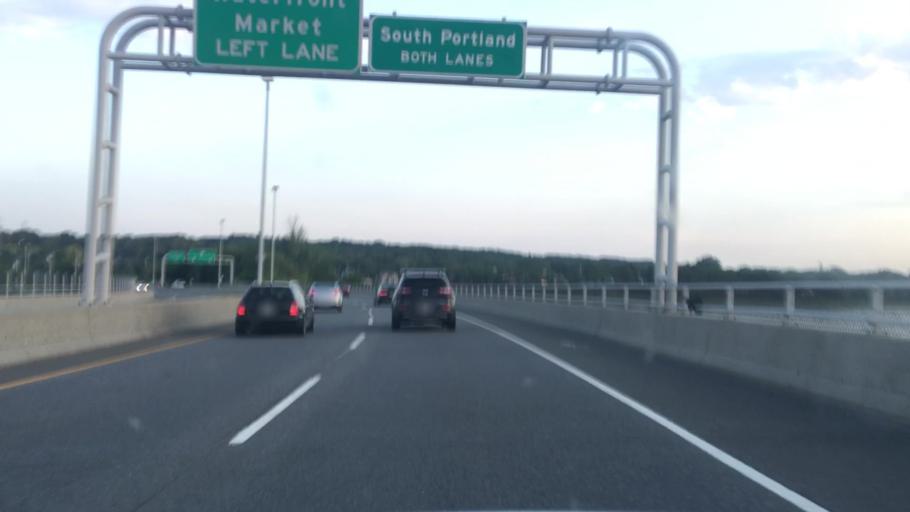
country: US
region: Maine
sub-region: Cumberland County
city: South Portland
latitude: 43.6370
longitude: -70.2590
